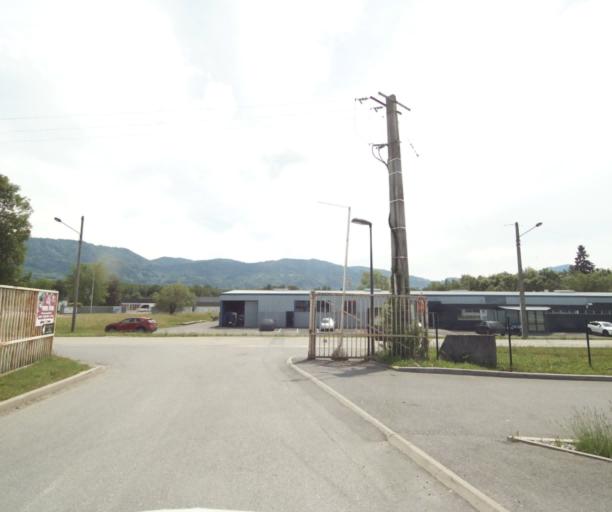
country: FR
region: Rhone-Alpes
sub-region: Departement de la Haute-Savoie
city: Perrignier
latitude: 46.3049
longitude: 6.4224
